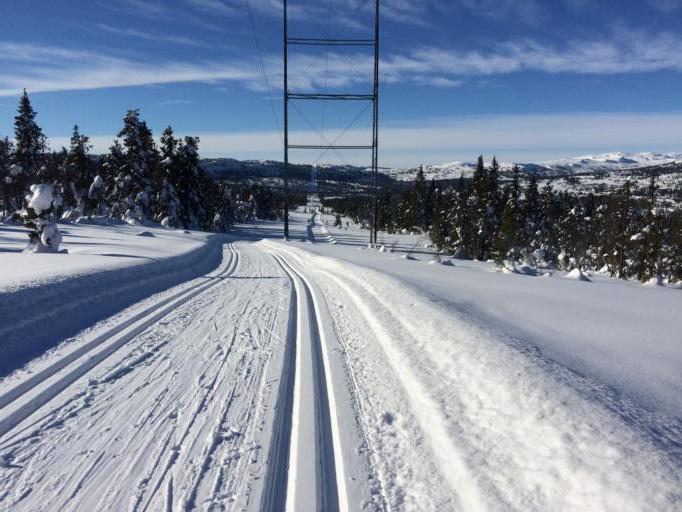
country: NO
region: Oppland
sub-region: Gausdal
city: Segalstad bru
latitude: 61.3139
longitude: 10.1055
